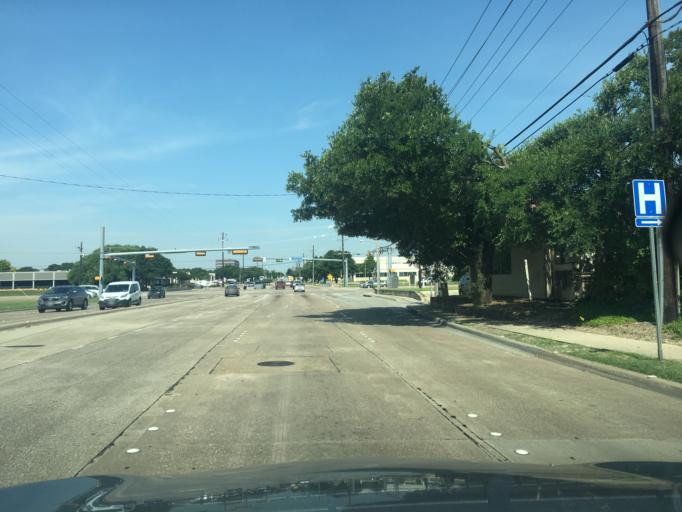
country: US
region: Texas
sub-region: Dallas County
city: Richardson
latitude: 32.9607
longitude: -96.6988
